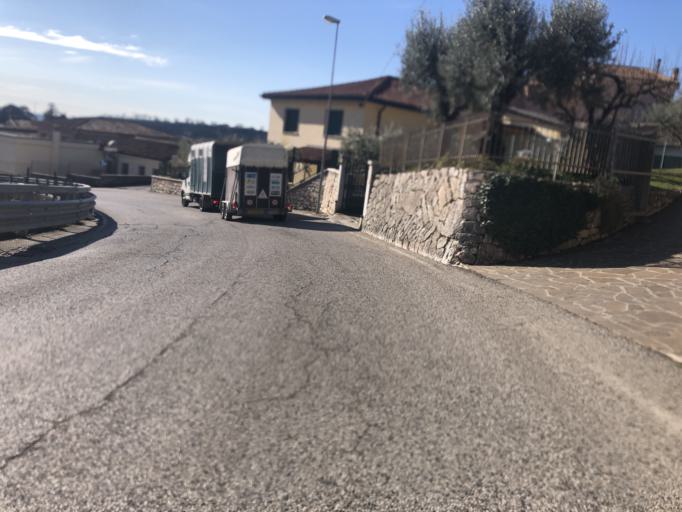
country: IT
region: Veneto
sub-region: Provincia di Verona
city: Sant'Ambrogio di Valpollicella
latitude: 45.5276
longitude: 10.8373
